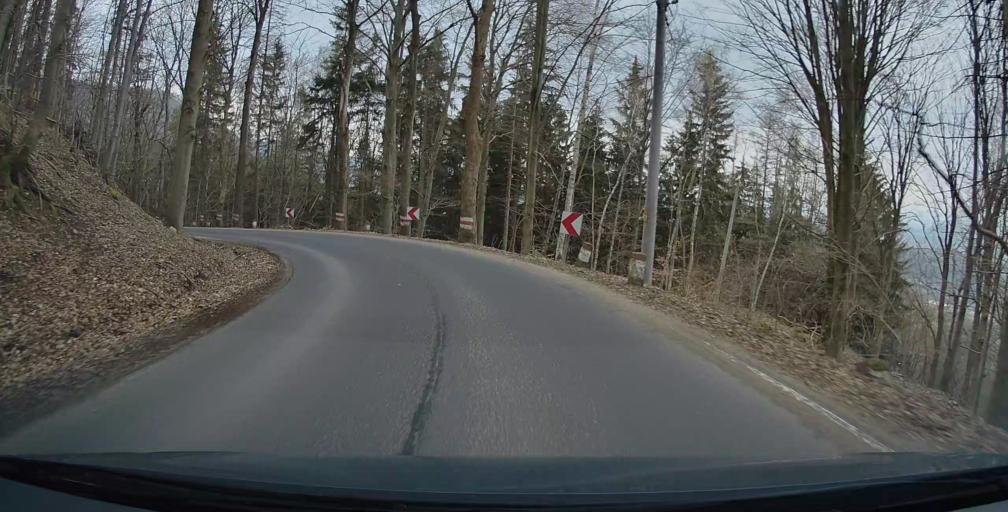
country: PL
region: Lower Silesian Voivodeship
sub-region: Powiat klodzki
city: Radkow
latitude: 50.4851
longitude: 16.3825
